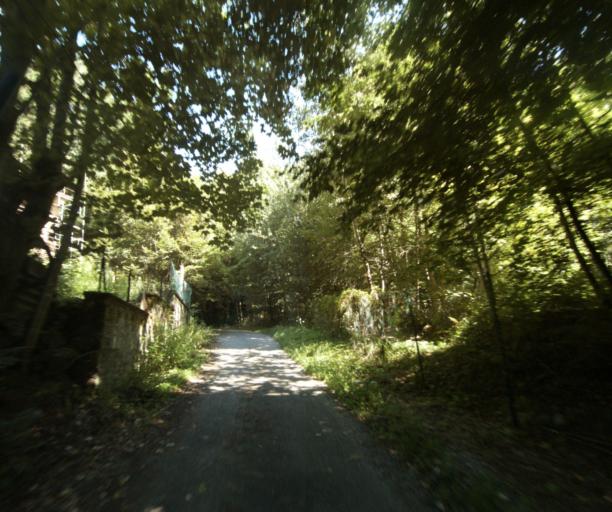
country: FR
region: Lorraine
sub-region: Departement des Vosges
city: Epinal
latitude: 48.1649
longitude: 6.4658
